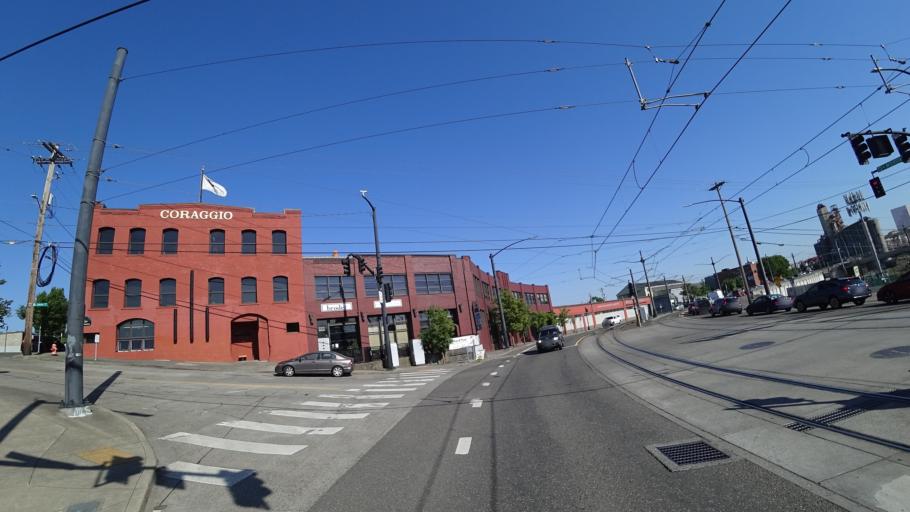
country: US
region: Oregon
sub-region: Multnomah County
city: Portland
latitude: 45.5394
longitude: -122.6751
